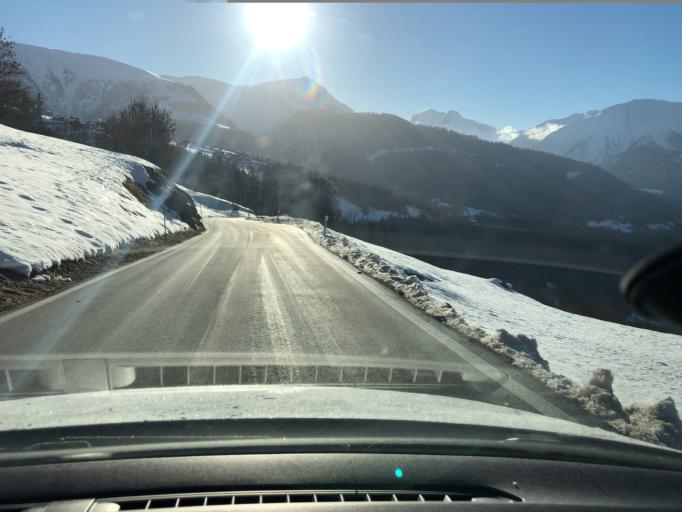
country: CH
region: Valais
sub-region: Goms District
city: Fiesch
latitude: 46.4326
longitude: 8.1476
